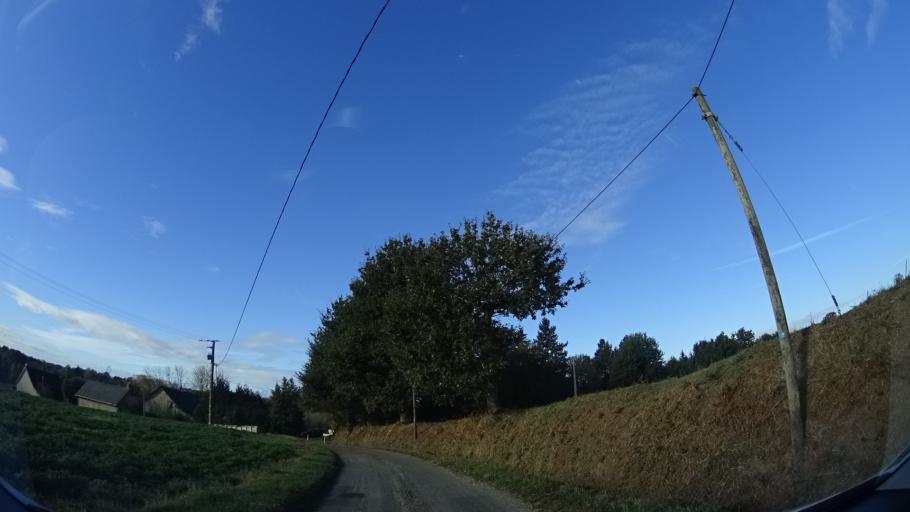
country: FR
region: Brittany
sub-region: Departement d'Ille-et-Vilaine
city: Geveze
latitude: 48.2023
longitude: -1.7819
